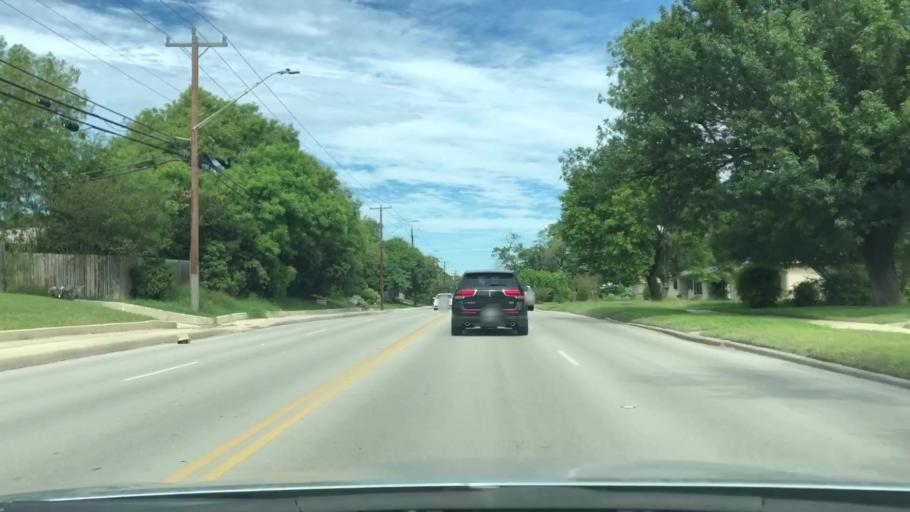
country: US
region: Texas
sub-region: Bexar County
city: Olmos Park
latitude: 29.5065
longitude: -98.4917
